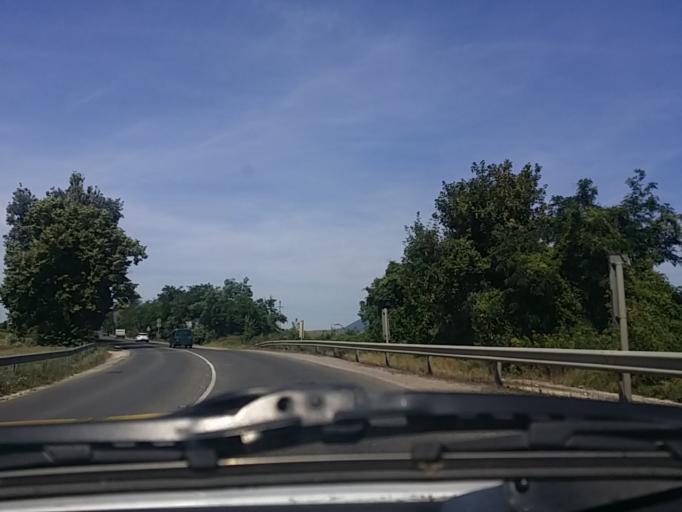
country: HU
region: Pest
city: Pilisborosjeno
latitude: 47.5984
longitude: 18.9655
